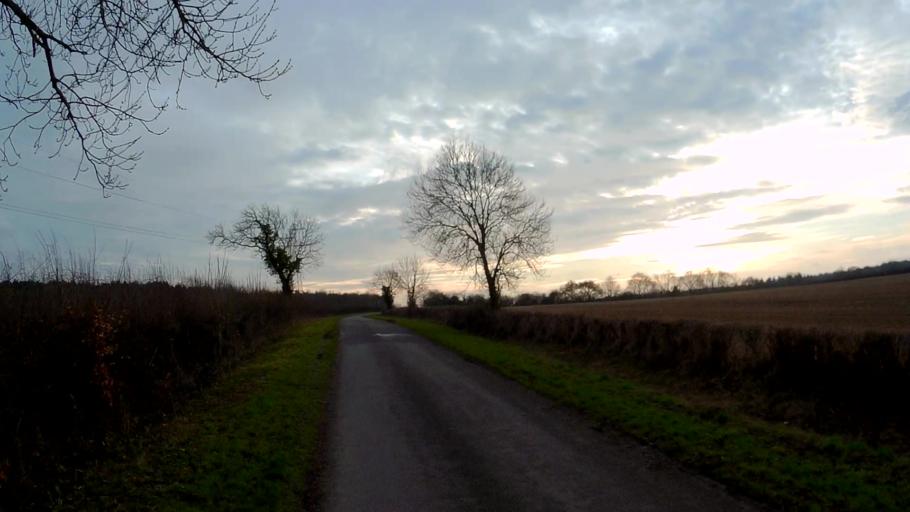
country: GB
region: England
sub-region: Lincolnshire
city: Bourne
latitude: 52.8254
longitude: -0.4057
